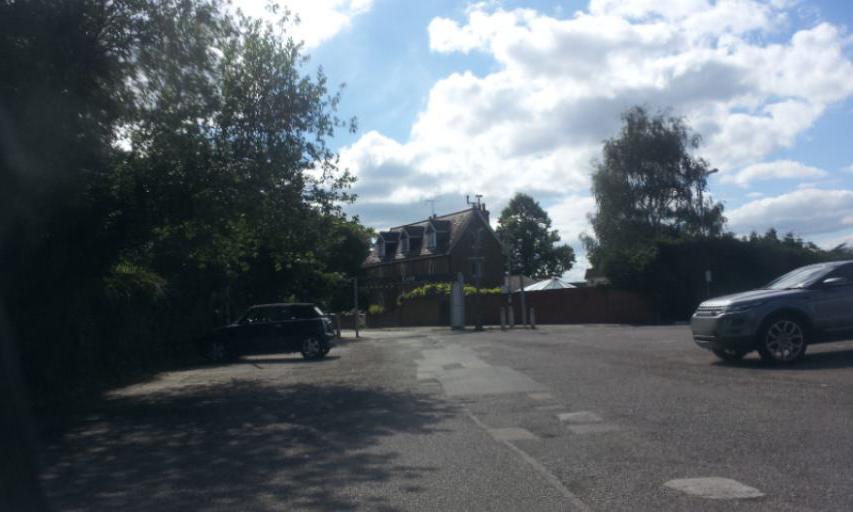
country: GB
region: England
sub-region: Kent
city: Marden
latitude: 51.1751
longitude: 0.4930
